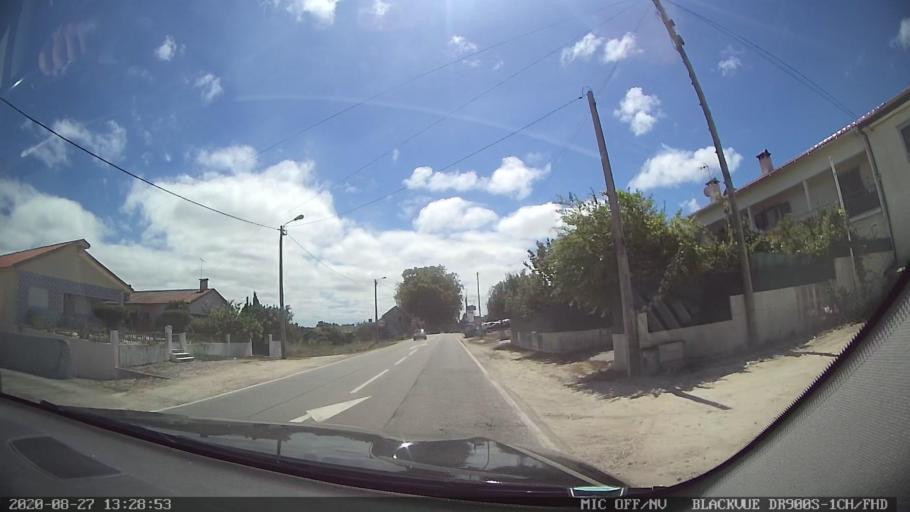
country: PT
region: Aveiro
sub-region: Vagos
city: Vagos
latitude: 40.5158
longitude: -8.6782
